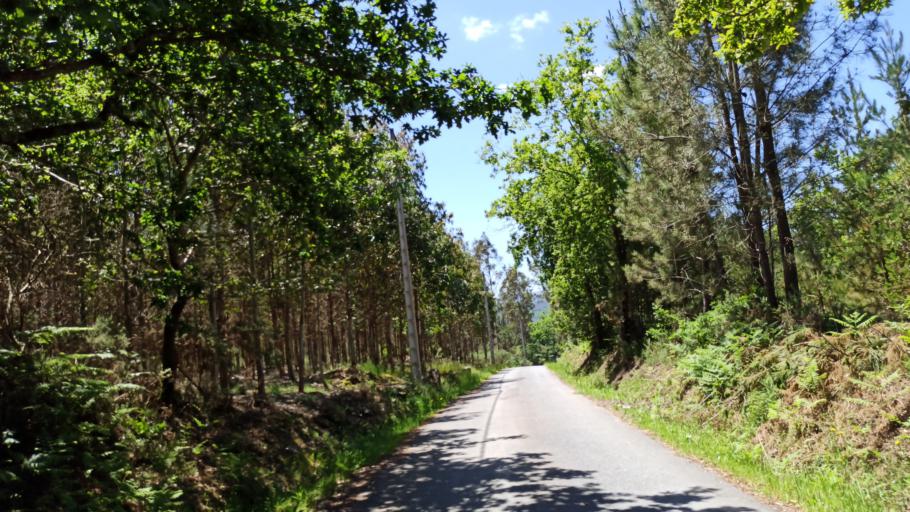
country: ES
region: Galicia
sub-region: Provincia da Coruna
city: Negreira
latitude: 42.9144
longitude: -8.7226
